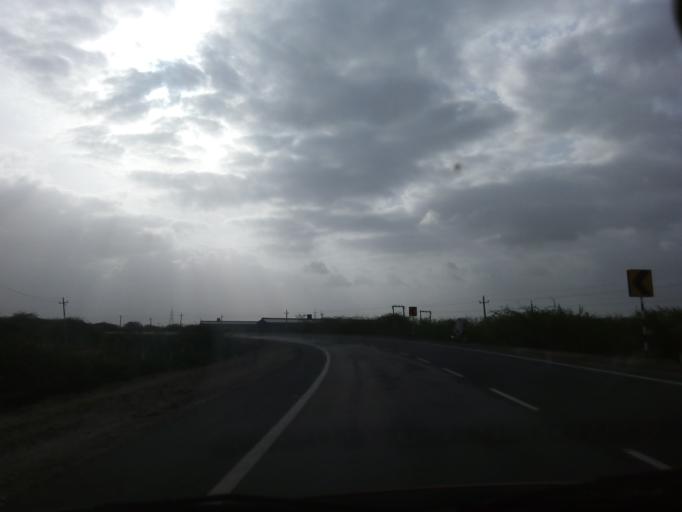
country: IN
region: Gujarat
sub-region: Kachchh
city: Anjar
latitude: 23.2924
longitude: 70.0944
